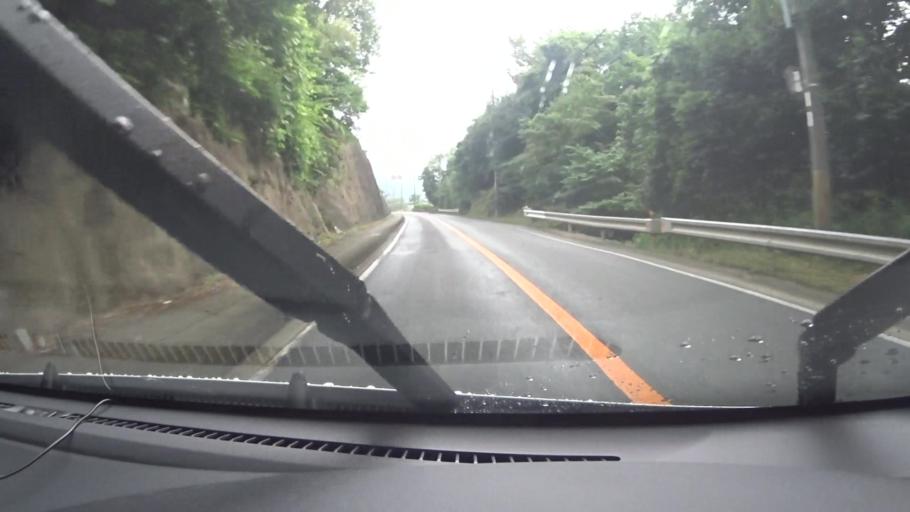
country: JP
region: Kyoto
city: Ayabe
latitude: 35.2950
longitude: 135.3294
